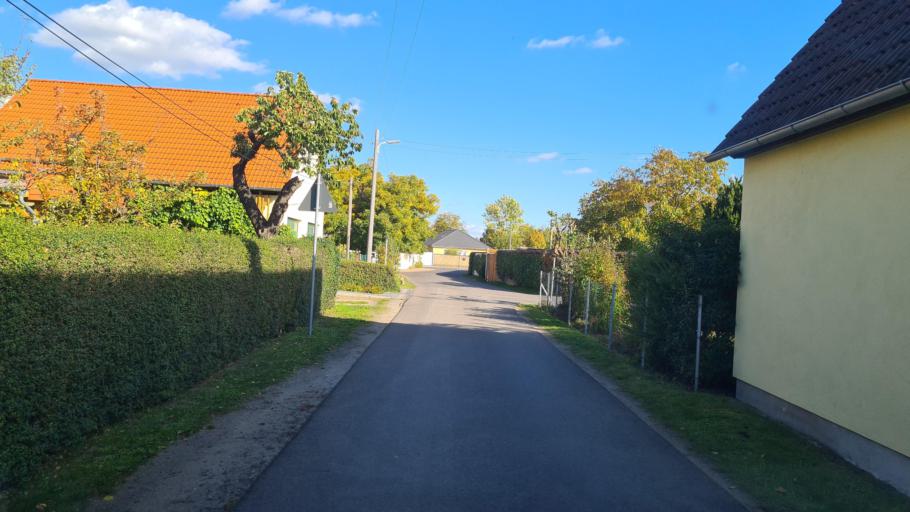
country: DE
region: Brandenburg
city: Cottbus
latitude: 51.7606
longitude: 14.2976
